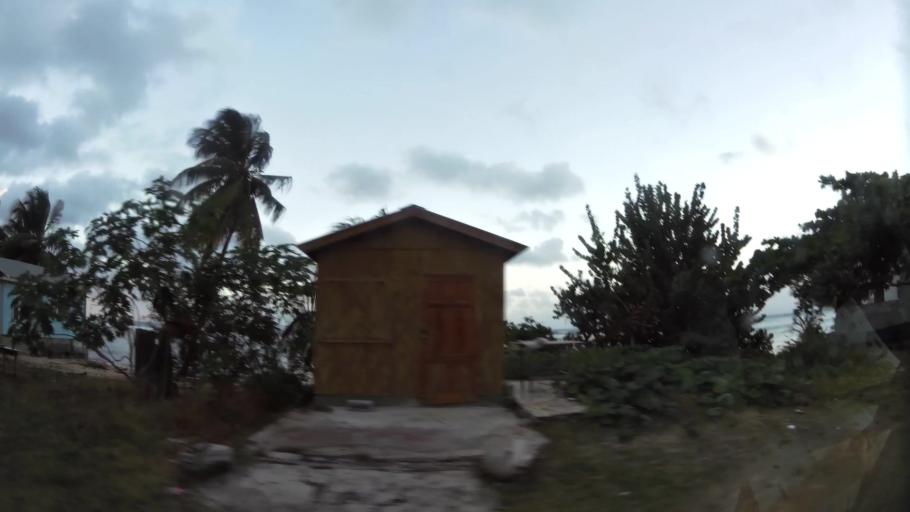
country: DM
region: Saint Andrew
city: Calibishie
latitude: 15.5929
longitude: -61.3495
